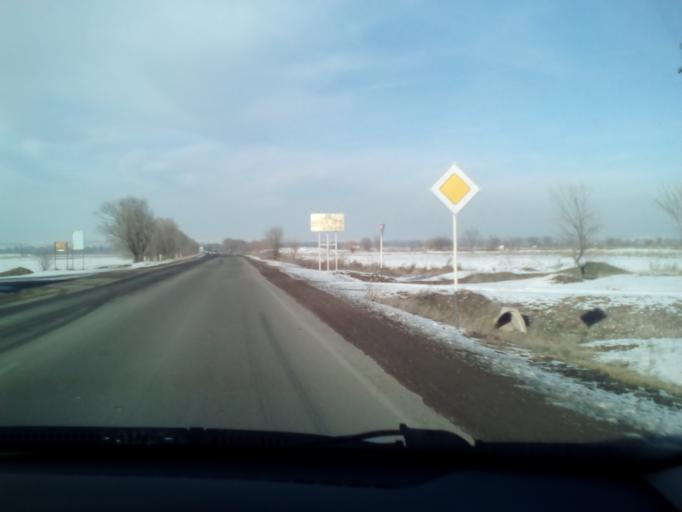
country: KZ
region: Almaty Oblysy
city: Burunday
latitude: 43.2056
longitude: 76.4150
